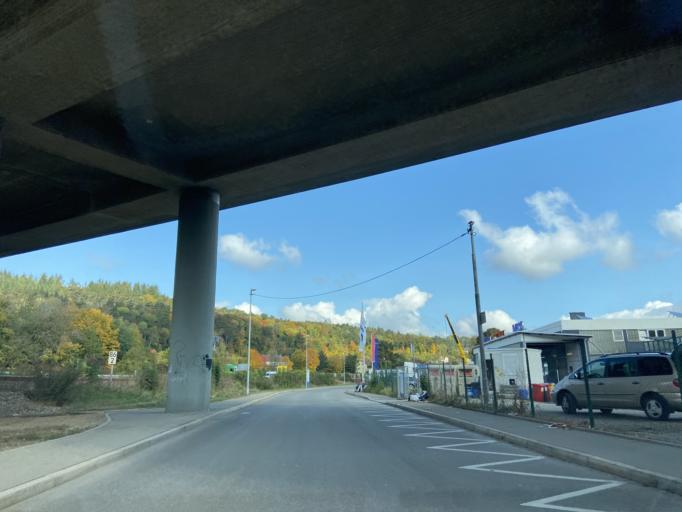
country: DE
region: Baden-Wuerttemberg
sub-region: Tuebingen Region
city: Sigmaringen
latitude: 48.0887
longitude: 9.2060
